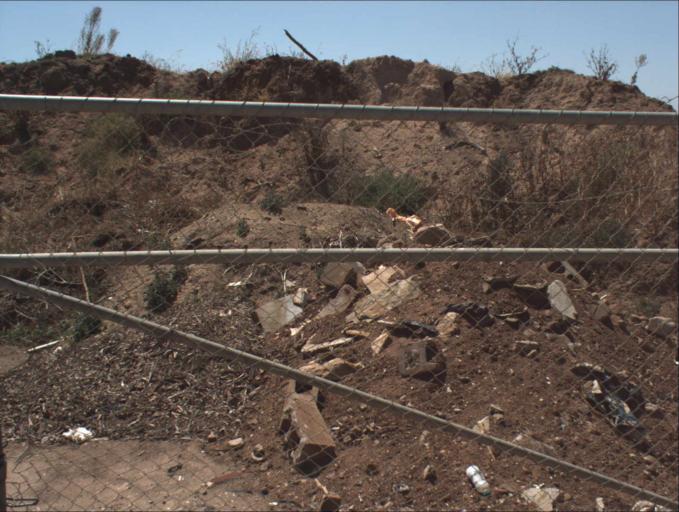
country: AU
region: South Australia
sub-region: Port Adelaide Enfield
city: Blair Athol
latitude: -34.8344
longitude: 138.5680
